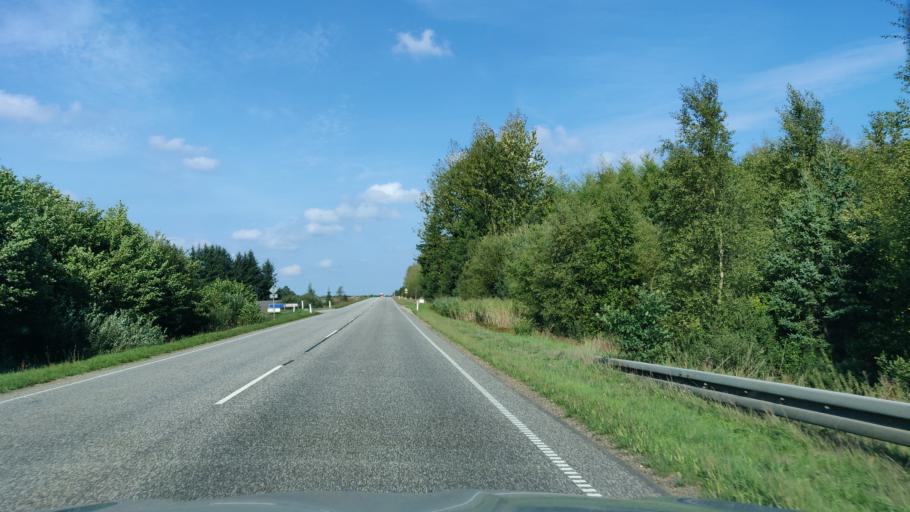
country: DK
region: Central Jutland
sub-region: Herning Kommune
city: Sunds
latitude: 56.3360
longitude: 8.9826
